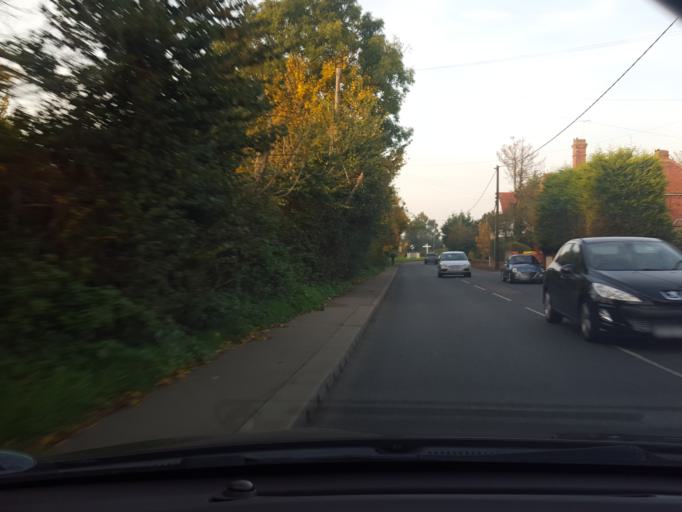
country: GB
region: England
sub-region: Essex
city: Saint Osyth
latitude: 51.8039
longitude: 1.0785
